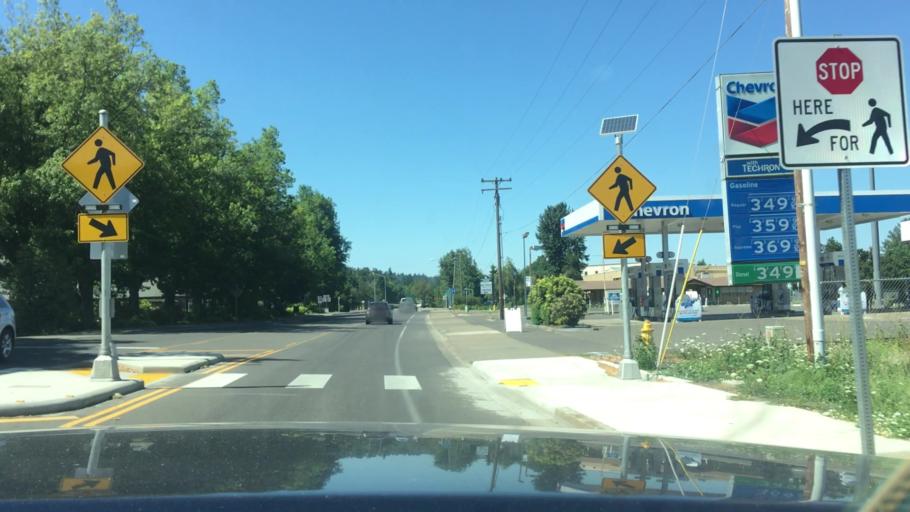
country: US
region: Oregon
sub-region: Lane County
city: Cottage Grove
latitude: 43.8010
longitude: -123.0399
